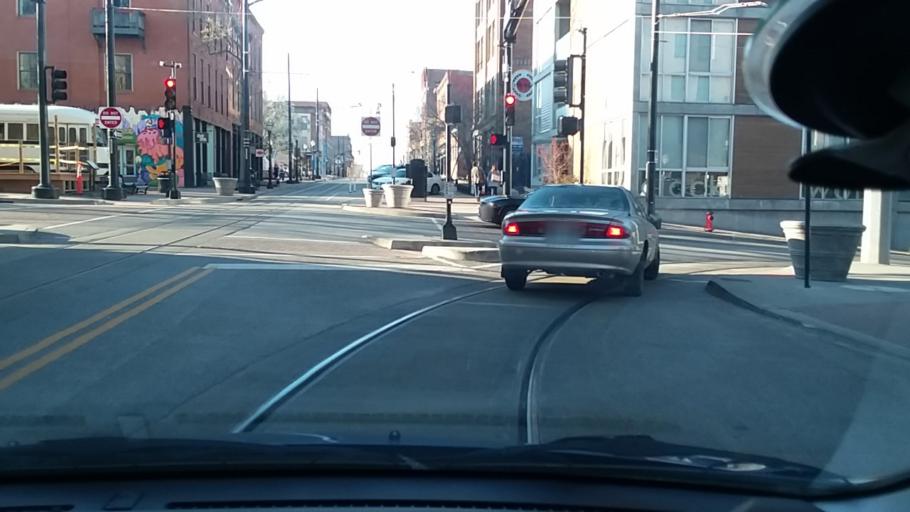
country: US
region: Missouri
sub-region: Jackson County
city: Kansas City
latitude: 39.1079
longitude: -94.5840
